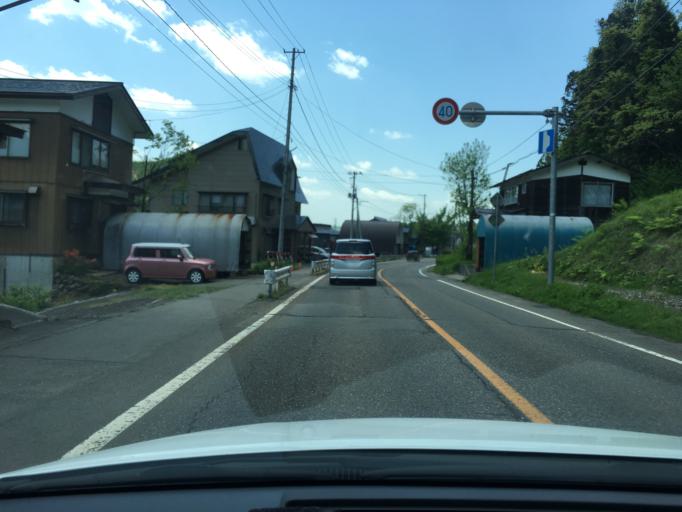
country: JP
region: Niigata
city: Tochio-honcho
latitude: 37.3068
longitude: 139.0094
